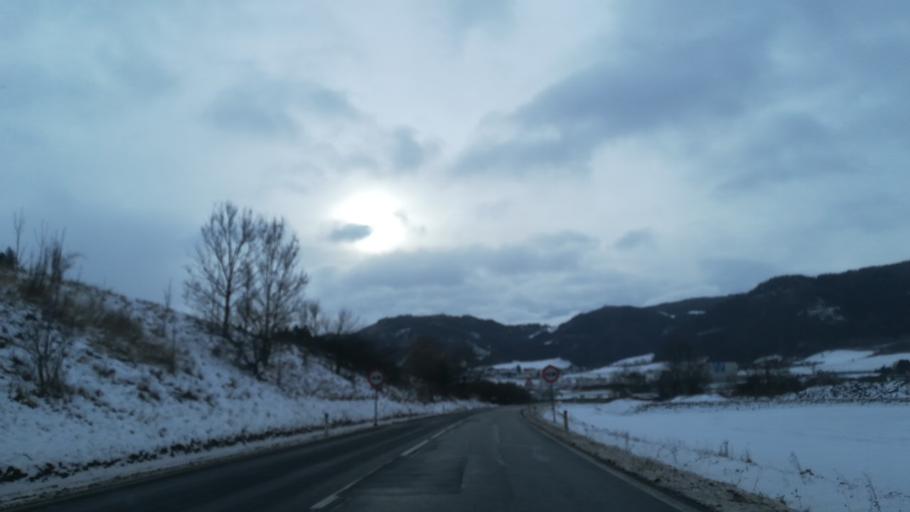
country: AT
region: Styria
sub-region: Politischer Bezirk Murtal
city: Sankt Peter ob Judenburg
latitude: 47.1933
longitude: 14.5986
